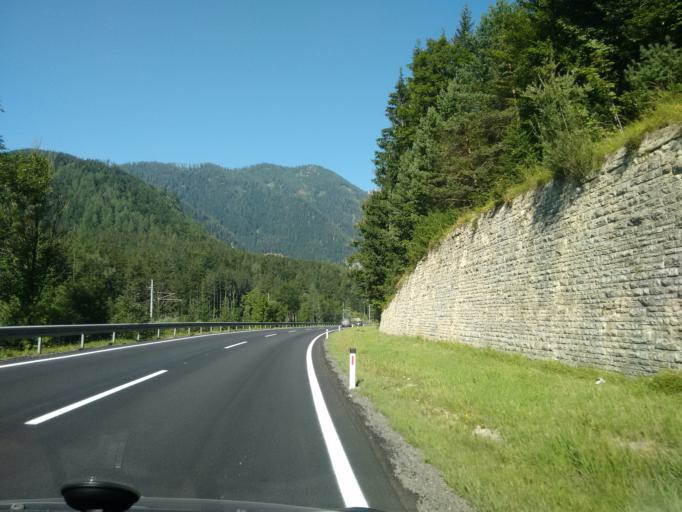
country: AT
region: Styria
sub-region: Politischer Bezirk Liezen
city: Bad Aussee
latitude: 47.5742
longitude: 13.8297
